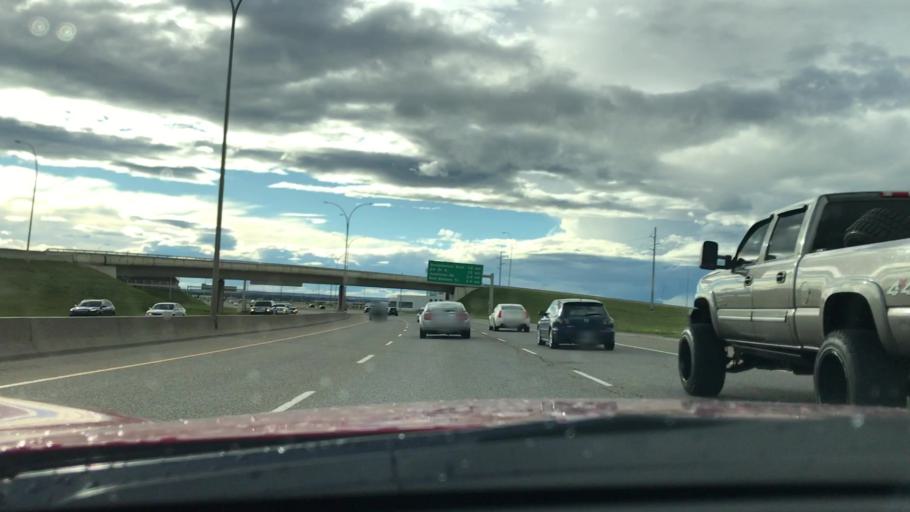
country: CA
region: Alberta
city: Calgary
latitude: 50.9437
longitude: -113.9800
